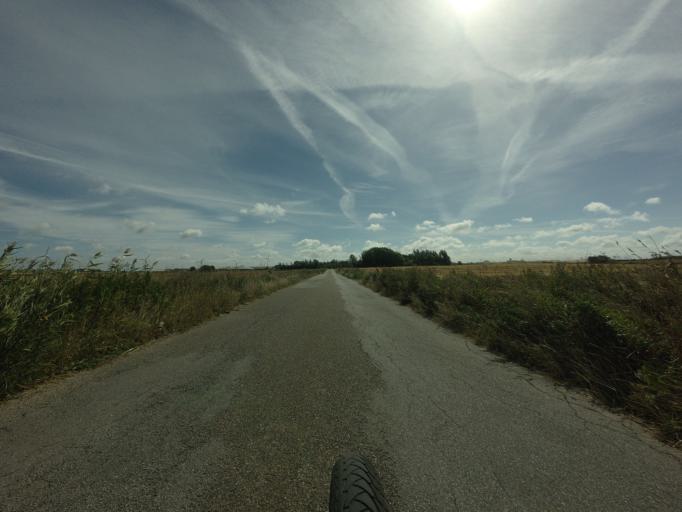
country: DK
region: North Denmark
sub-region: Hjorring Kommune
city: Vra
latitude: 57.3404
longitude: 9.8052
